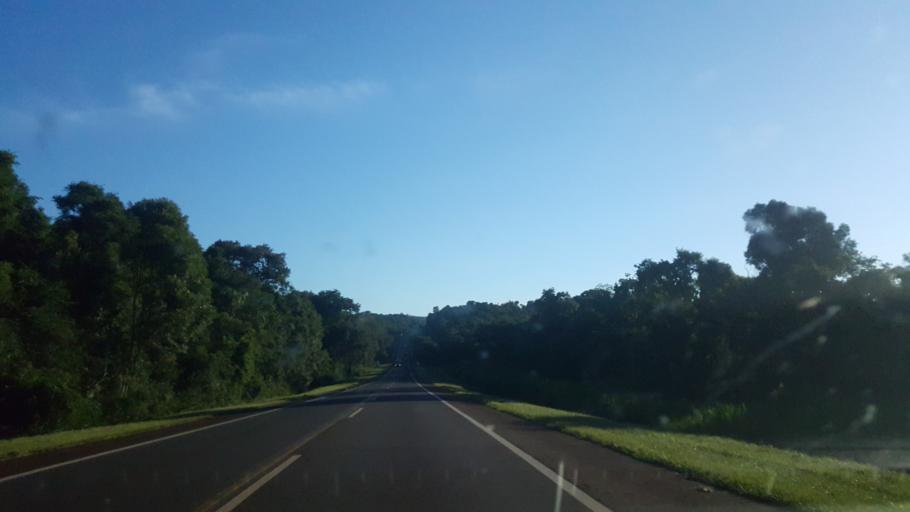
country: AR
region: Misiones
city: El Alcazar
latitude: -26.7050
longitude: -54.8425
